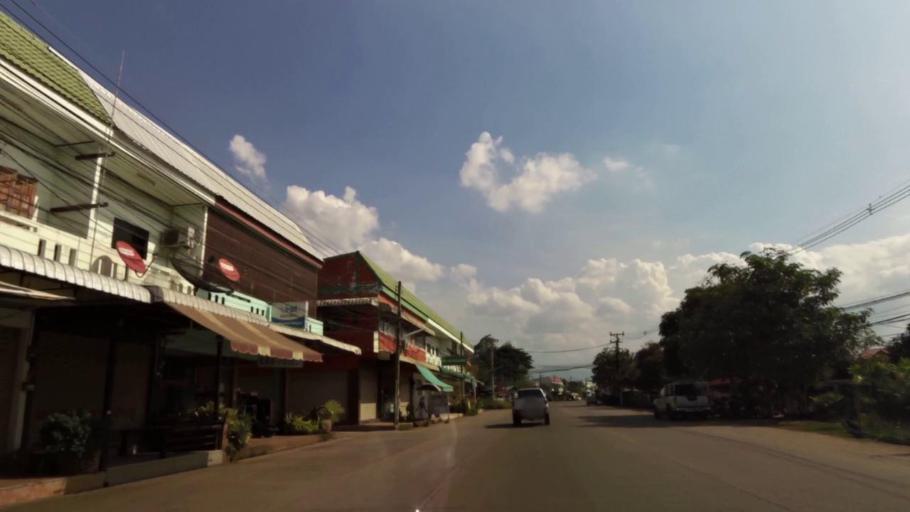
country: TH
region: Phrae
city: Phrae
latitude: 18.1246
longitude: 100.1518
